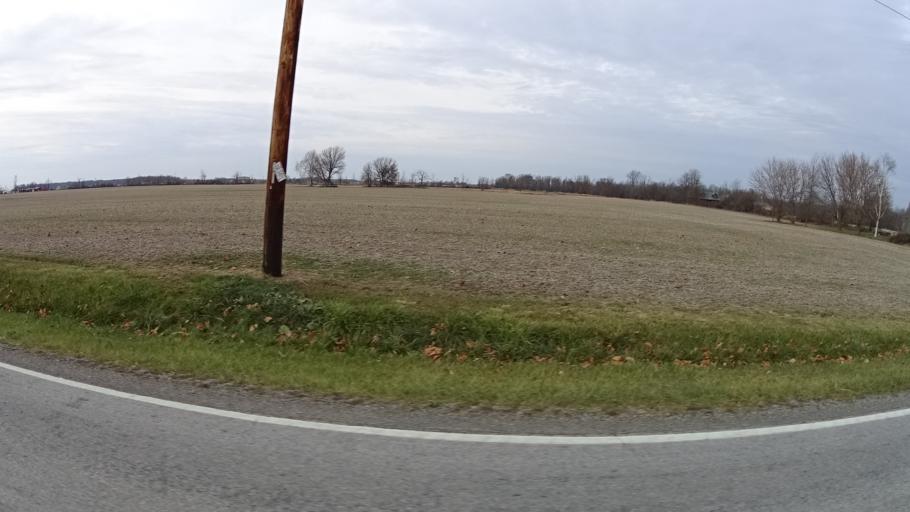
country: US
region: Ohio
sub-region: Lorain County
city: Wellington
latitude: 41.1516
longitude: -82.1695
